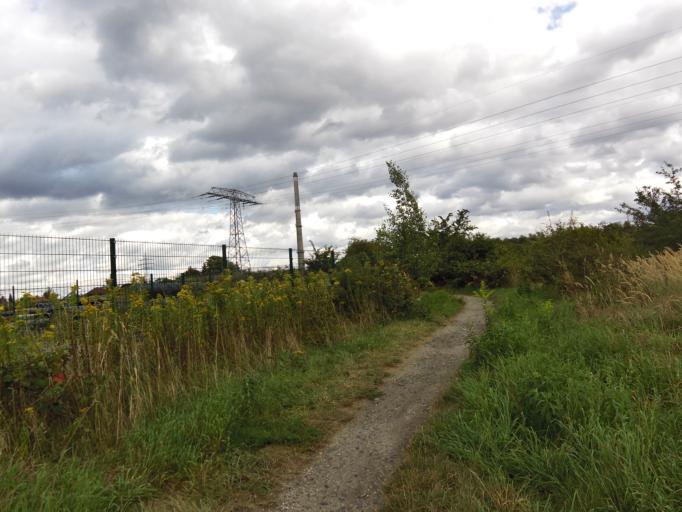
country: DE
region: Saxony
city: Markranstadt
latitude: 51.3468
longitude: 12.2848
